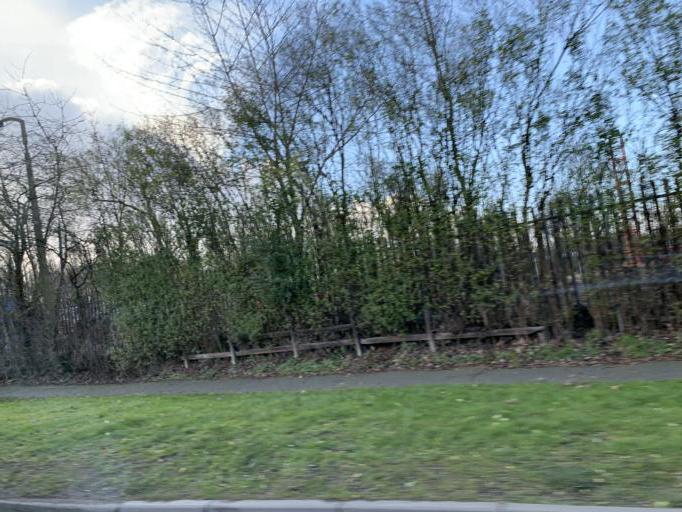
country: GB
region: England
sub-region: City and Borough of Wakefield
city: Ferrybridge
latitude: 53.7148
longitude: -1.2712
